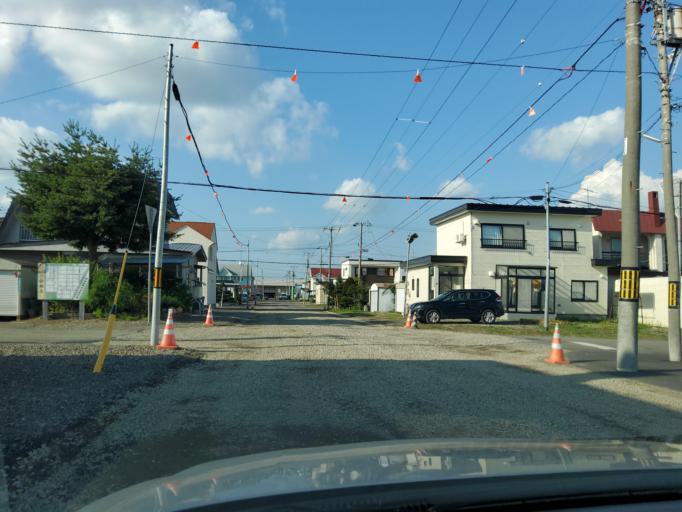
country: JP
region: Hokkaido
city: Obihiro
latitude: 42.8848
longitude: 143.2001
